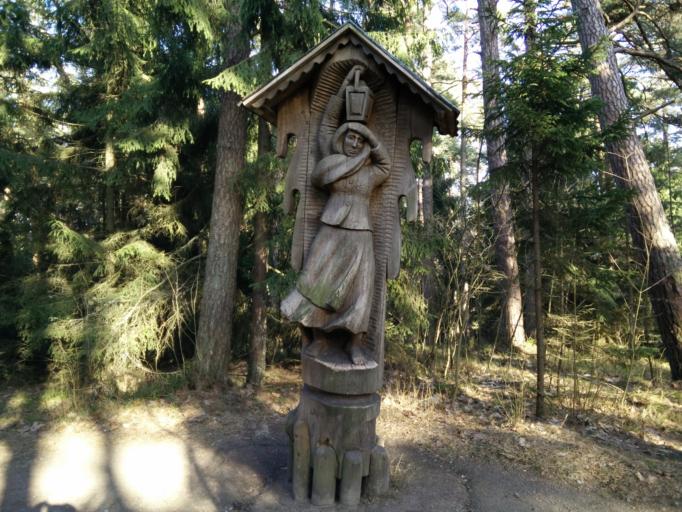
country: LT
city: Neringa
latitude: 55.5360
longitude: 21.1109
